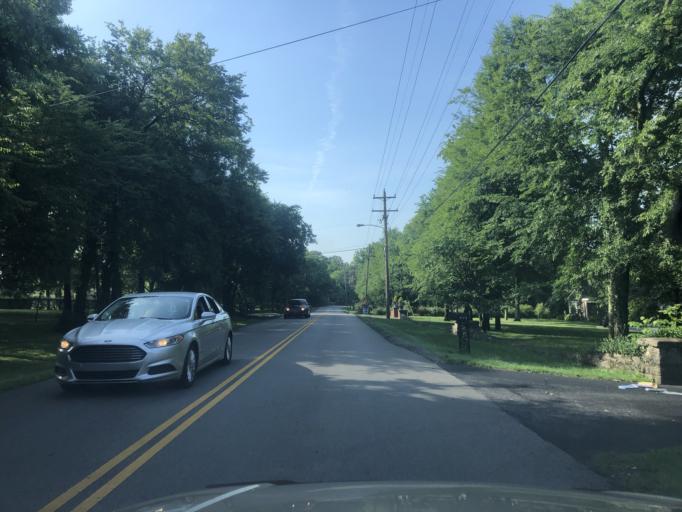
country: US
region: Tennessee
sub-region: Davidson County
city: Lakewood
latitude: 36.2251
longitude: -86.7109
